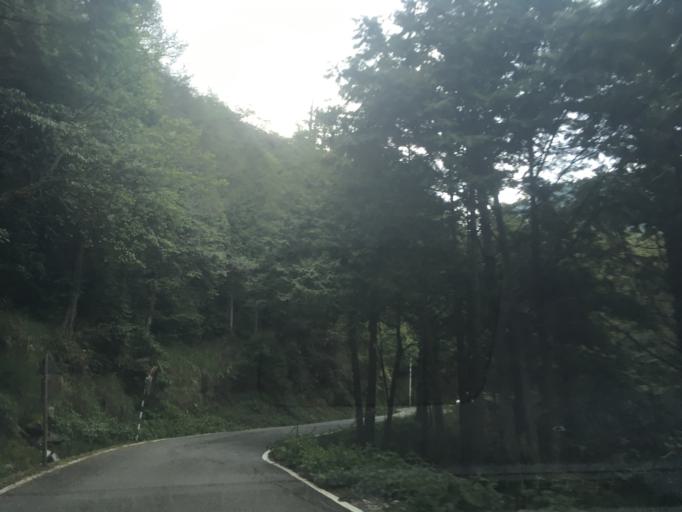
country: TW
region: Taiwan
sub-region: Nantou
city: Puli
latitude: 24.2616
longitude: 121.0160
